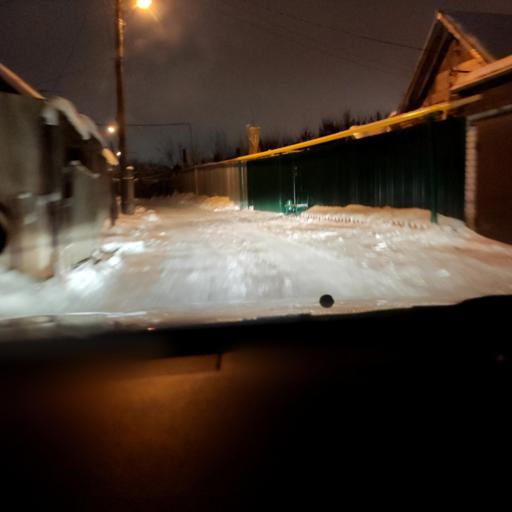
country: RU
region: Samara
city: Samara
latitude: 53.1826
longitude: 50.2287
